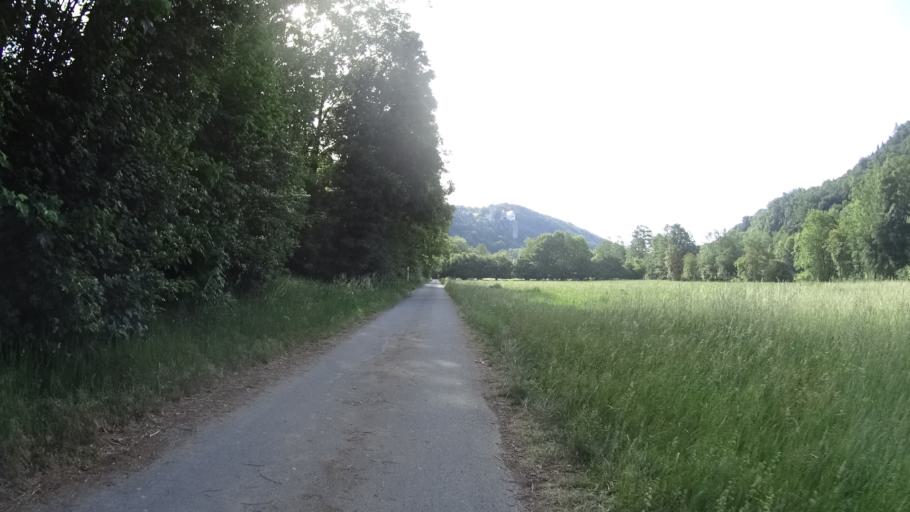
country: DE
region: Bavaria
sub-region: Lower Bavaria
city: Riedenburg
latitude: 48.9531
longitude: 11.7285
